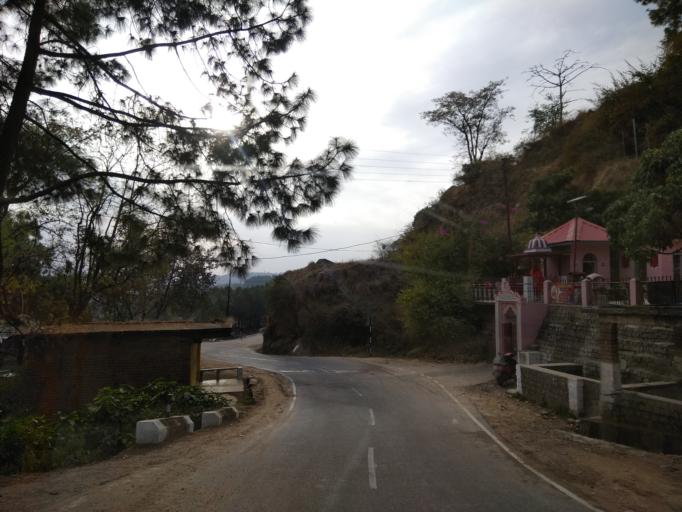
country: IN
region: Himachal Pradesh
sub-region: Kangra
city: Palampur
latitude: 32.1111
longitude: 76.4879
